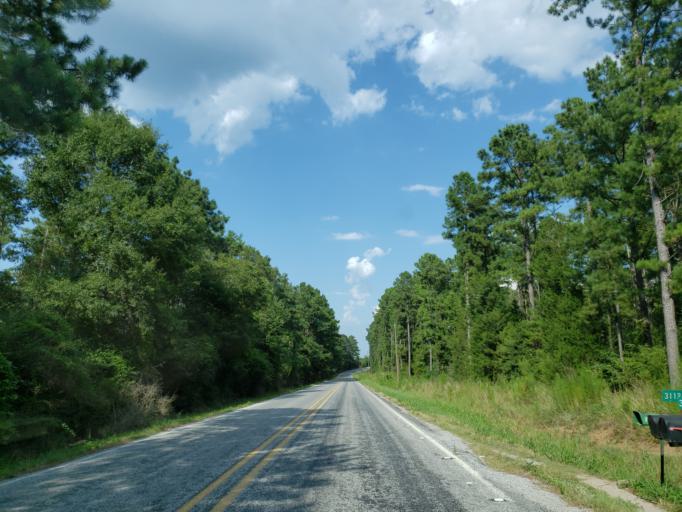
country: US
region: Mississippi
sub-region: Jones County
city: Ellisville
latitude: 31.6214
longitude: -89.3748
